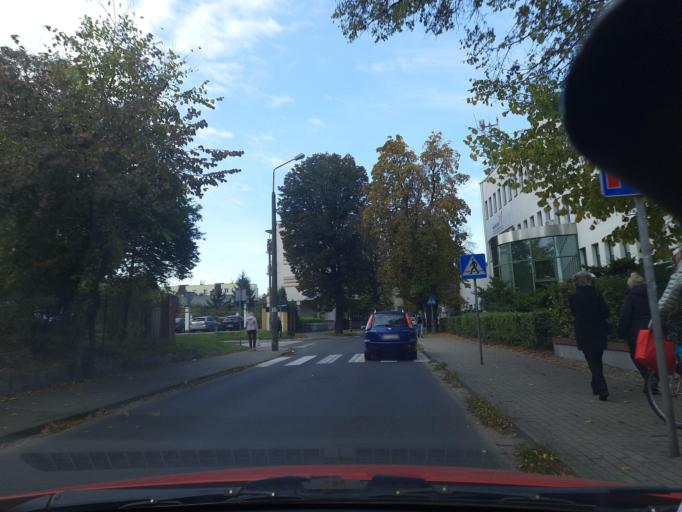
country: PL
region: Kujawsko-Pomorskie
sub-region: Torun
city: Torun
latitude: 53.0240
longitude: 18.6082
